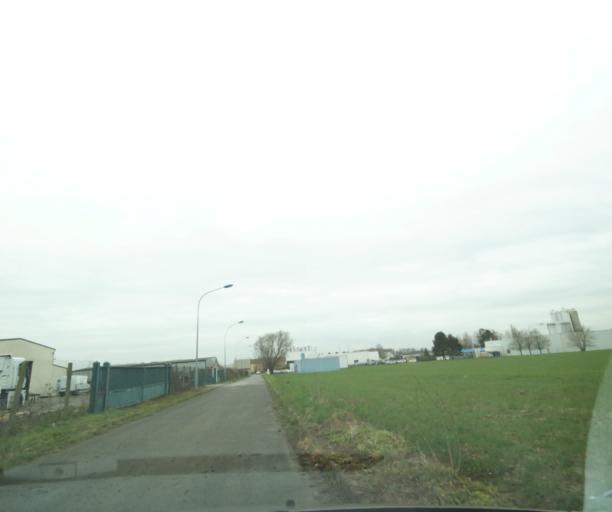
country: FR
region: Picardie
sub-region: Departement de l'Oise
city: Noyon
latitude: 49.5773
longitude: 3.0266
